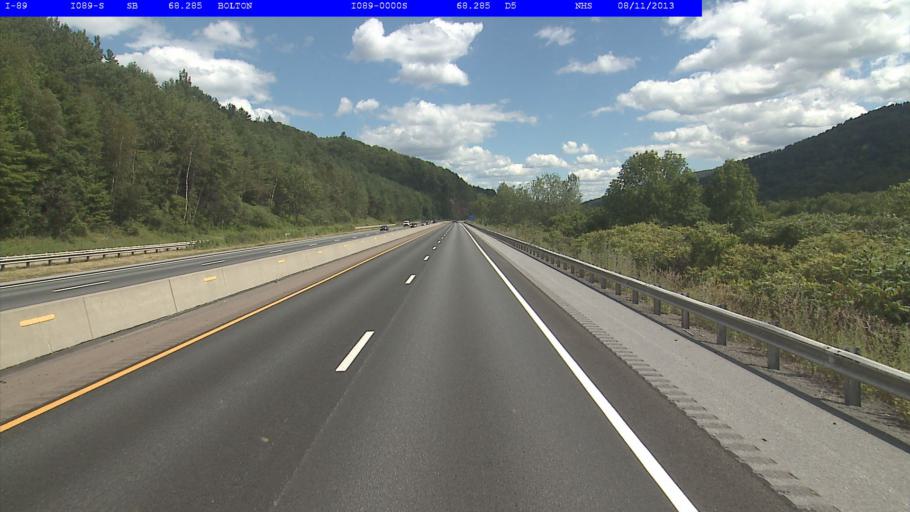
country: US
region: Vermont
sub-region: Washington County
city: Waterbury
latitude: 44.3619
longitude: -72.8354
